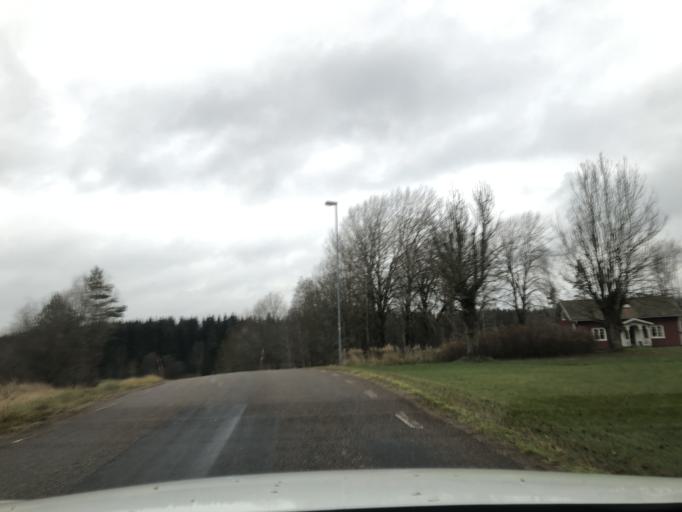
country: SE
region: Vaestra Goetaland
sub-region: Ulricehamns Kommun
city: Ulricehamn
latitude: 57.8671
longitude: 13.5491
